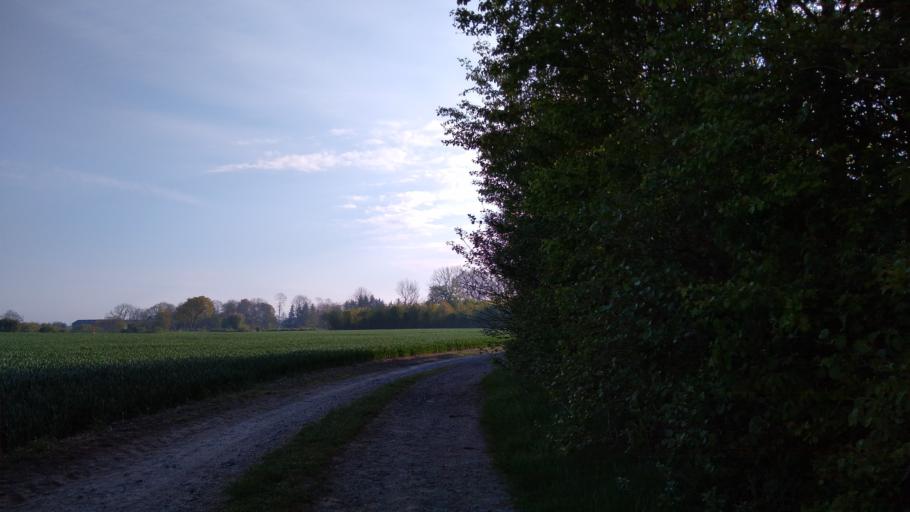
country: DK
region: South Denmark
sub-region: Fredericia Kommune
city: Snoghoj
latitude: 55.5707
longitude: 9.6915
